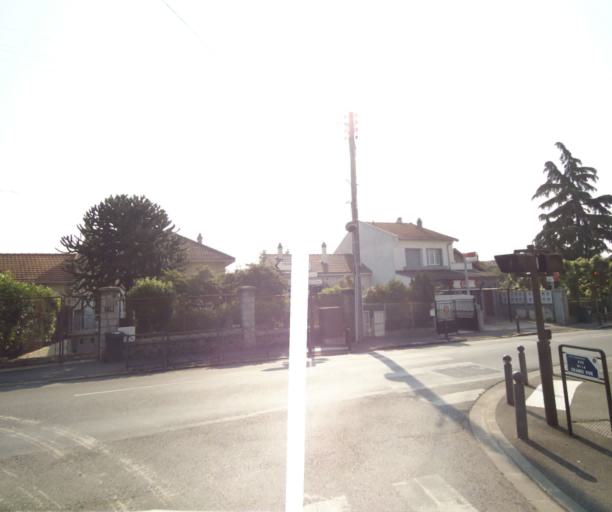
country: FR
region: Ile-de-France
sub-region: Departement du Val-d'Oise
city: Sannois
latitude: 48.9605
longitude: 2.2379
